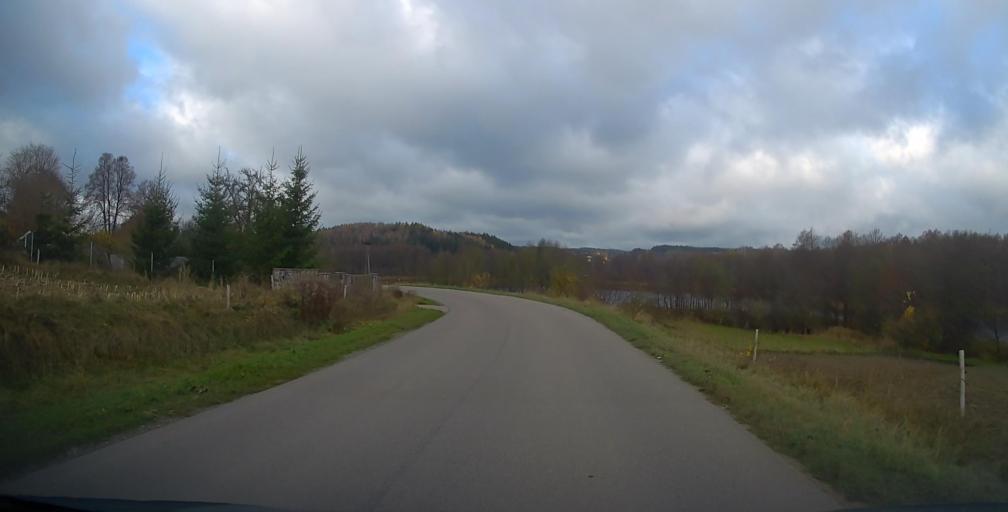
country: PL
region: Podlasie
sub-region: Suwalki
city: Suwalki
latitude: 54.2706
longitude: 22.9210
